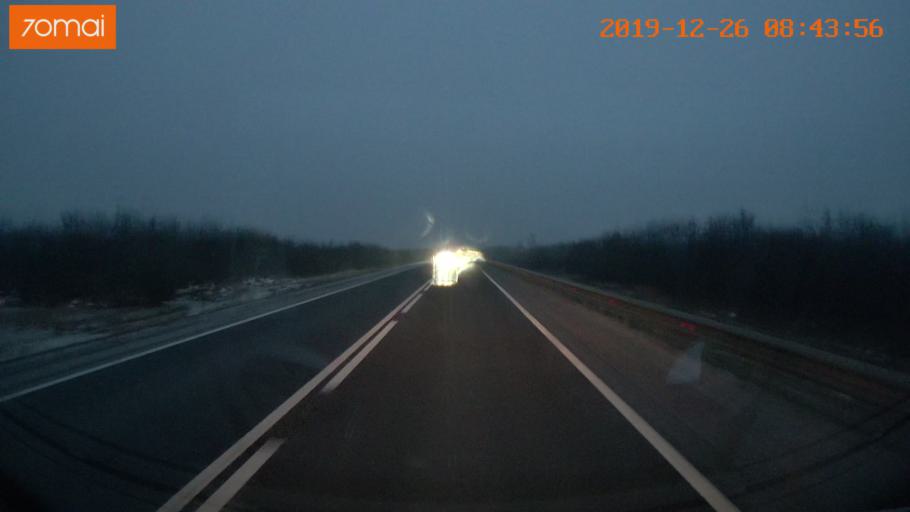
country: RU
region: Jaroslavl
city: Prechistoye
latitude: 58.5791
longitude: 40.3509
